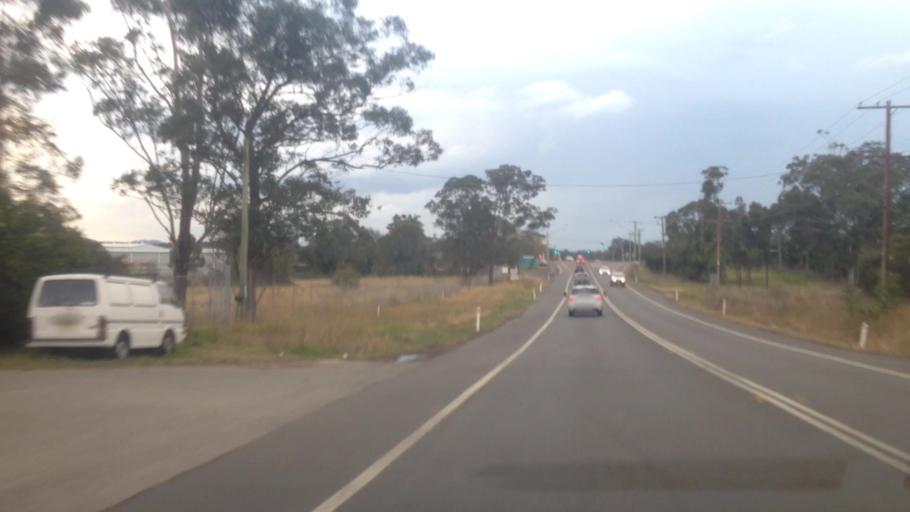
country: AU
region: New South Wales
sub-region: Wyong Shire
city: Tuggerawong
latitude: -33.2686
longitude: 151.4543
